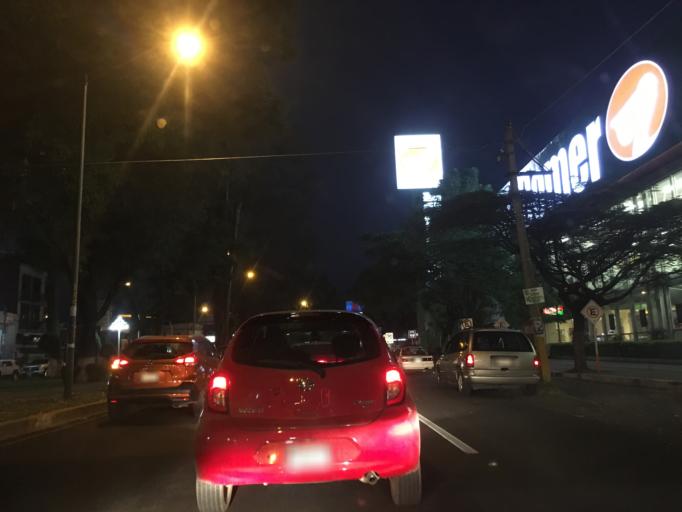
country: MX
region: Michoacan
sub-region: Uruapan
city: Uruapan
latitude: 19.4009
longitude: -102.0555
